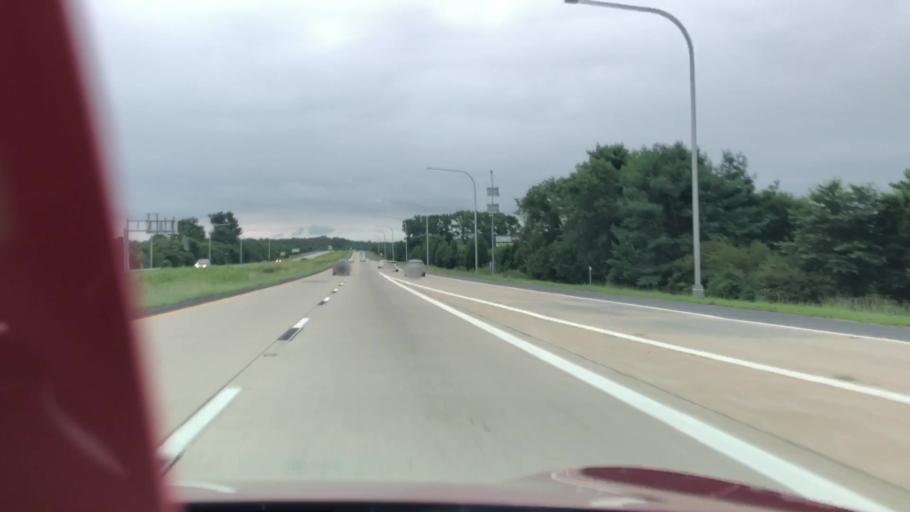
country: US
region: Delaware
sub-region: Kent County
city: Smyrna
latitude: 39.2787
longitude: -75.5872
